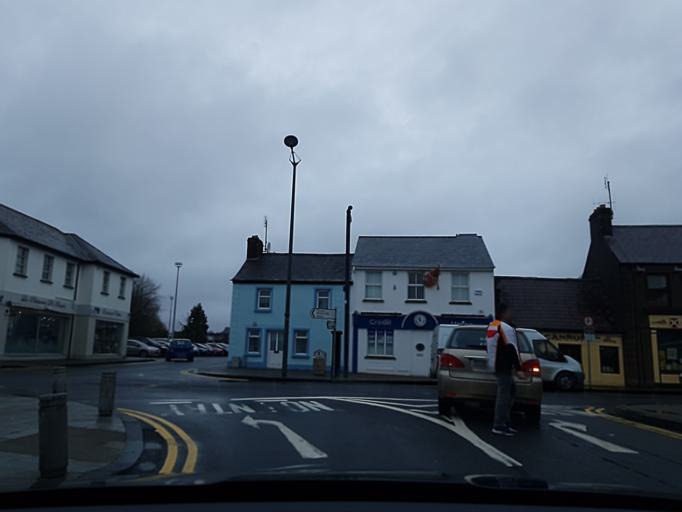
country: IE
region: Connaught
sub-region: Maigh Eo
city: Castlebar
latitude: 53.8563
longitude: -9.3004
